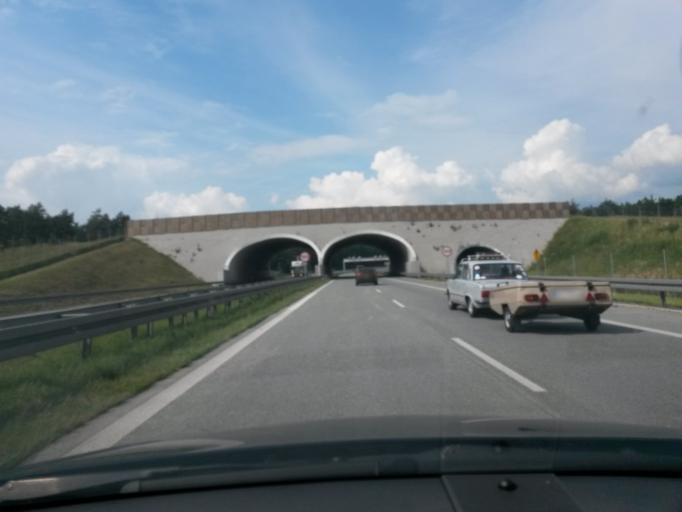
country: PL
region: Lodz Voivodeship
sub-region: Powiat tomaszowski
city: Lubochnia
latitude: 51.5775
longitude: 20.0290
